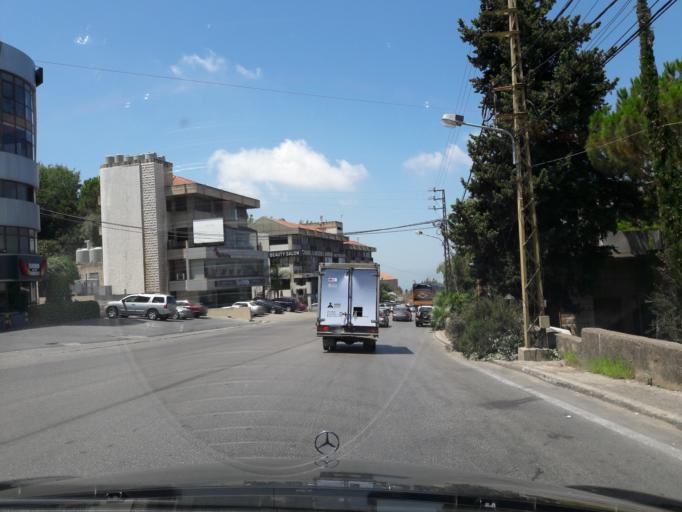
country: LB
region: Mont-Liban
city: Djounie
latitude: 33.9210
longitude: 35.6342
